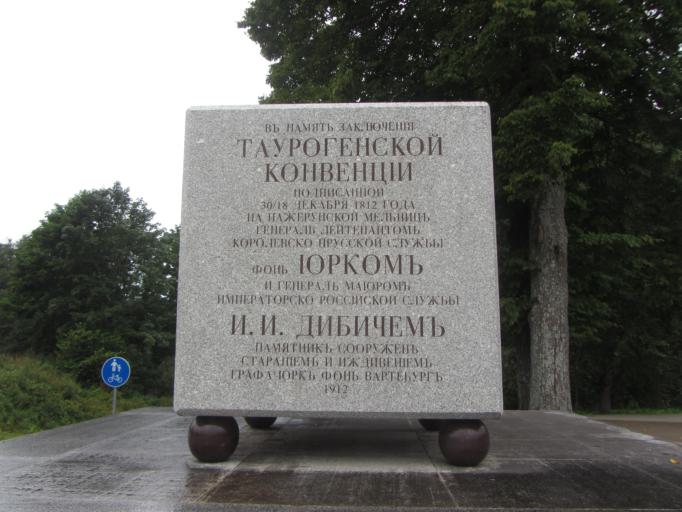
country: LT
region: Taurages apskritis
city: Taurage
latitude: 55.2277
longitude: 22.2237
